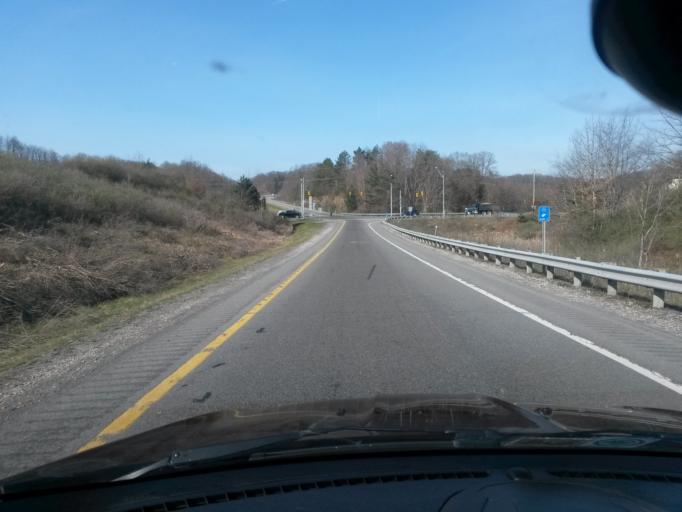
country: US
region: West Virginia
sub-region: Raleigh County
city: Bradley
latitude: 37.8523
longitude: -81.1957
